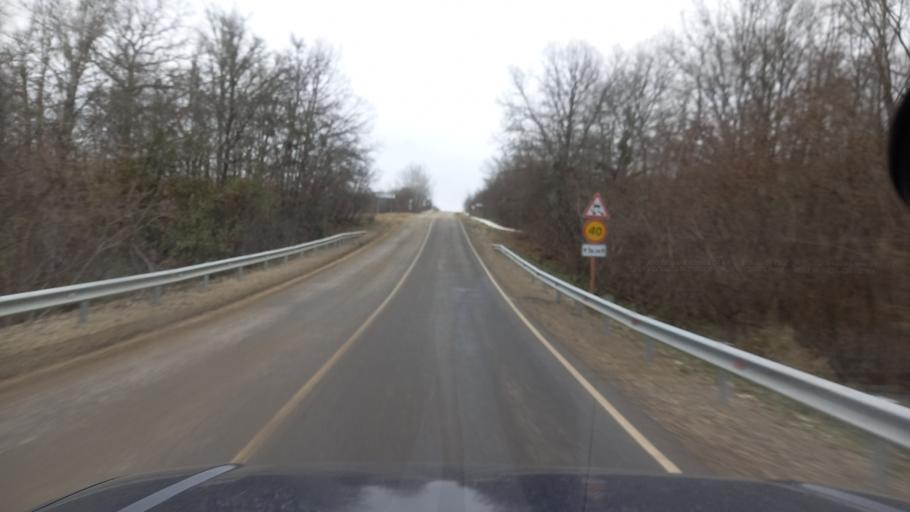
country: RU
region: Krasnodarskiy
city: Saratovskaya
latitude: 44.5457
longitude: 39.2816
